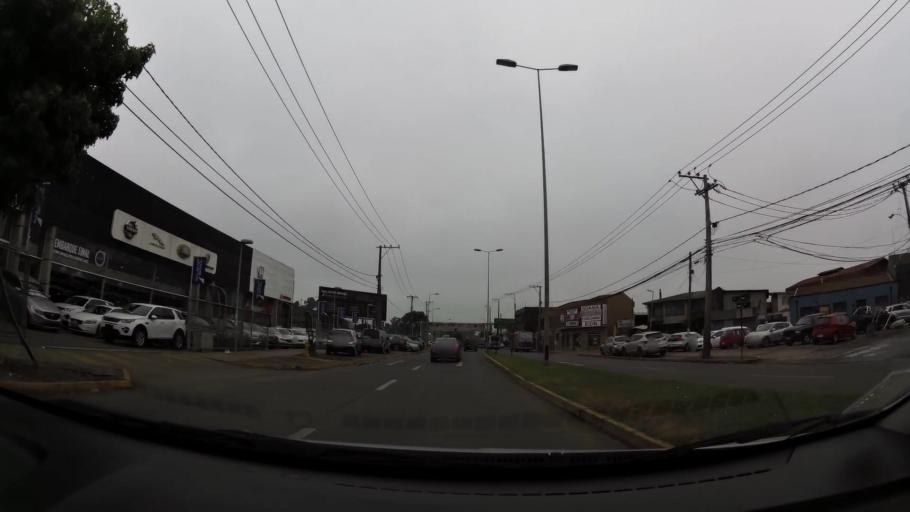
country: CL
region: Biobio
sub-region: Provincia de Concepcion
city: Concepcion
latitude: -36.8236
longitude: -73.0628
